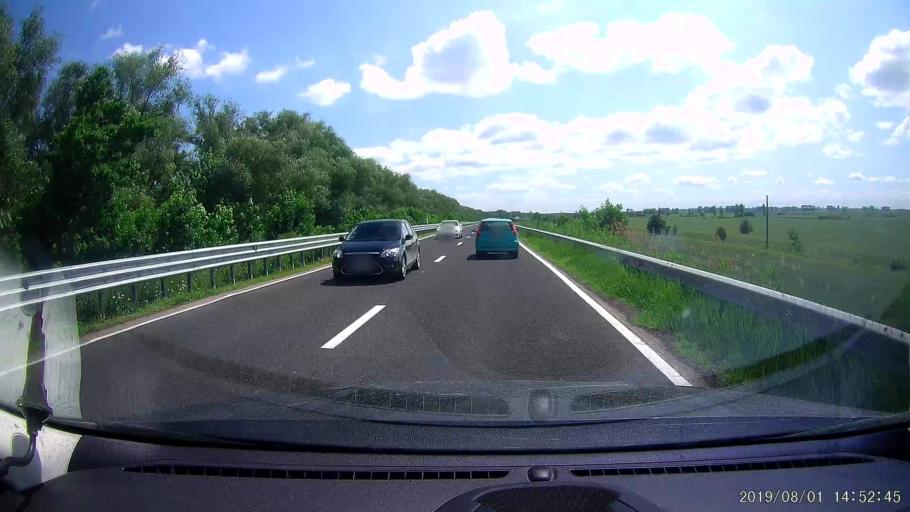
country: RO
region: Braila
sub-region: Comuna Vadeni
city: Vadeni
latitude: 45.3492
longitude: 28.0088
